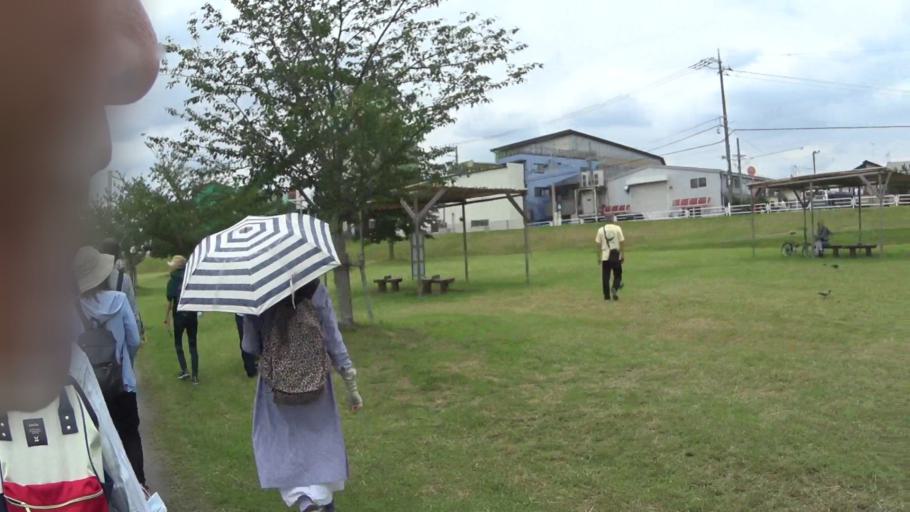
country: JP
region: Tokyo
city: Urayasu
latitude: 35.7109
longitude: 139.8397
